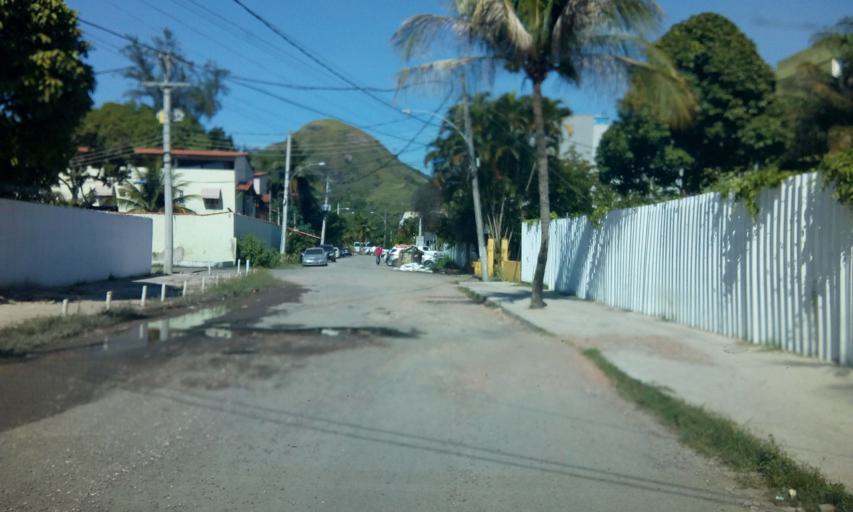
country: BR
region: Rio de Janeiro
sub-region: Nilopolis
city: Nilopolis
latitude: -23.0277
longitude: -43.4785
